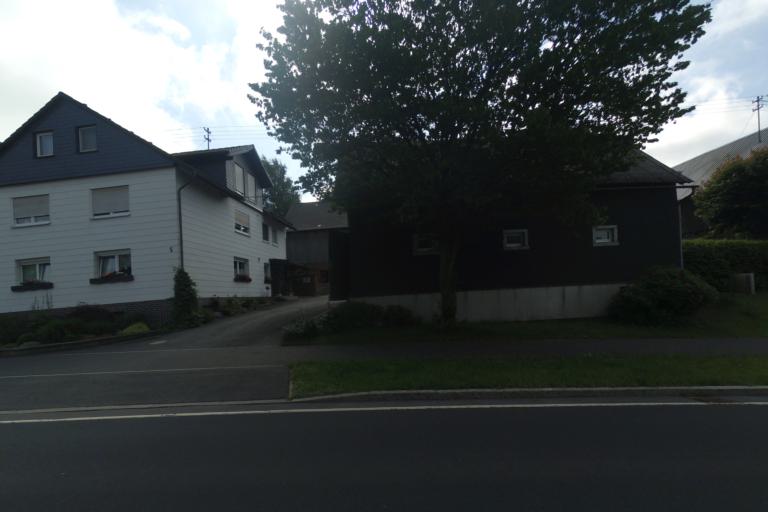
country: DE
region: Bavaria
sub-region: Upper Franconia
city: Teuschnitz
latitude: 50.4314
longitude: 11.3604
